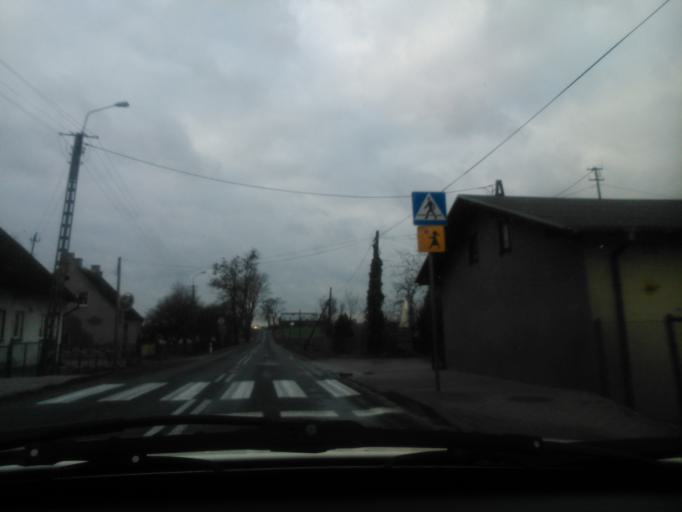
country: PL
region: Kujawsko-Pomorskie
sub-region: Powiat brodnicki
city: Bartniczka
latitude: 53.2494
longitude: 19.5676
